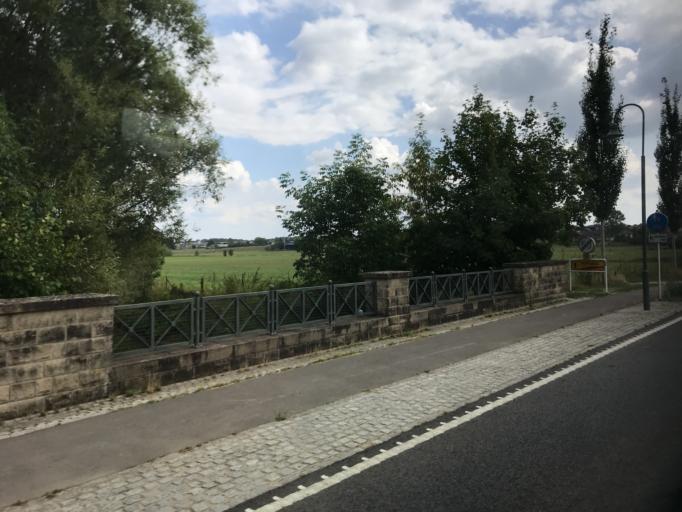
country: LU
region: Luxembourg
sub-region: Canton d'Esch-sur-Alzette
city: Bettembourg
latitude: 49.5271
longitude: 6.1212
